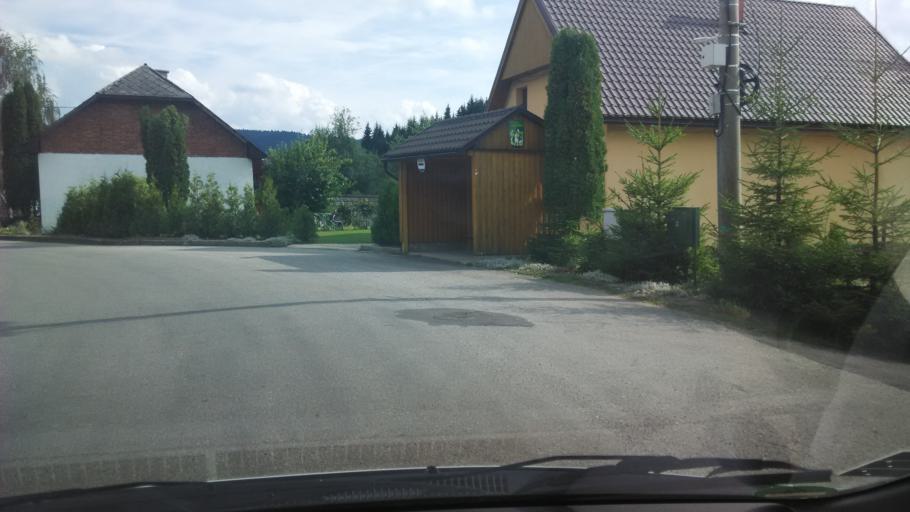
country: SK
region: Banskobystricky
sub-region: Okres Ziar nad Hronom
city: Kremnica
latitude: 48.7234
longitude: 18.9428
